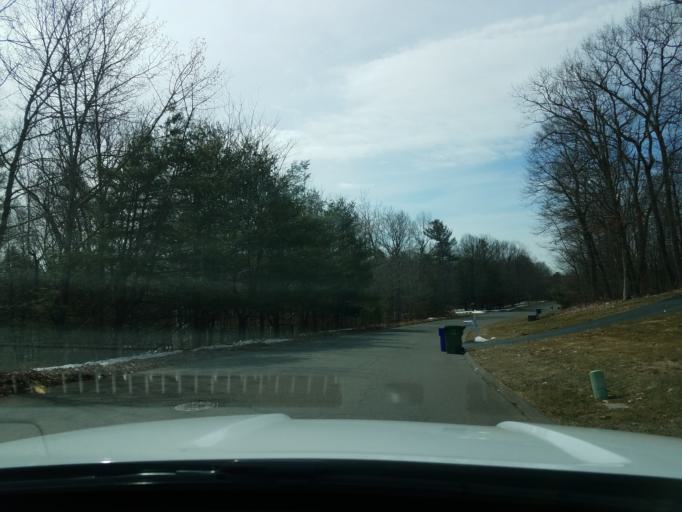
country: US
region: Connecticut
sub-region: Hartford County
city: Collinsville
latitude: 41.8066
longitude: -72.9117
